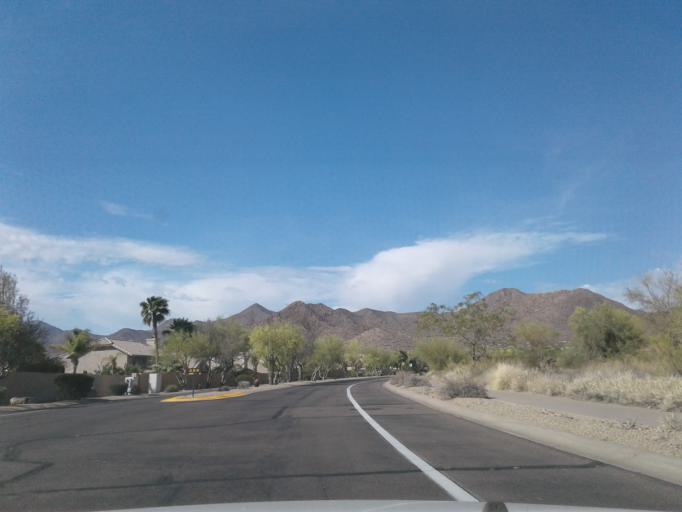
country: US
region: Arizona
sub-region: Maricopa County
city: Fountain Hills
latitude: 33.5845
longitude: -111.8002
